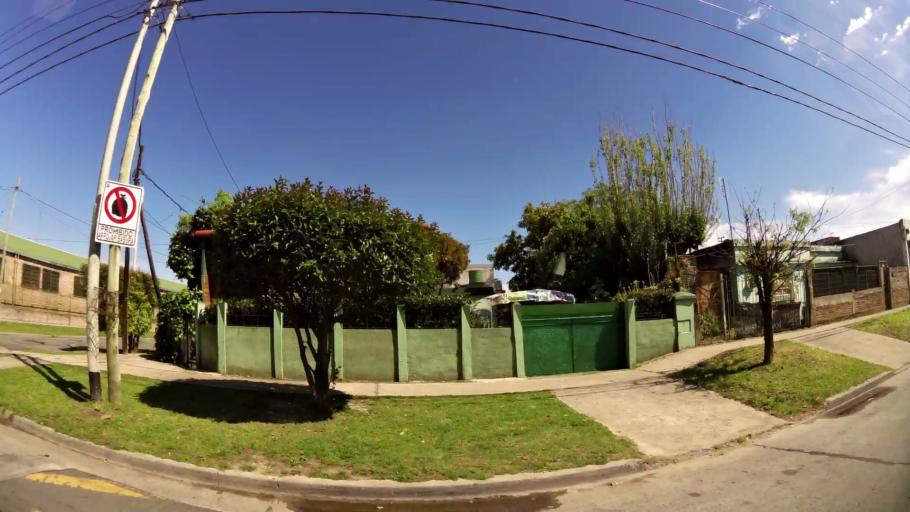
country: AR
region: Buenos Aires
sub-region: Partido de Quilmes
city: Quilmes
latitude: -34.6910
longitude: -58.3027
